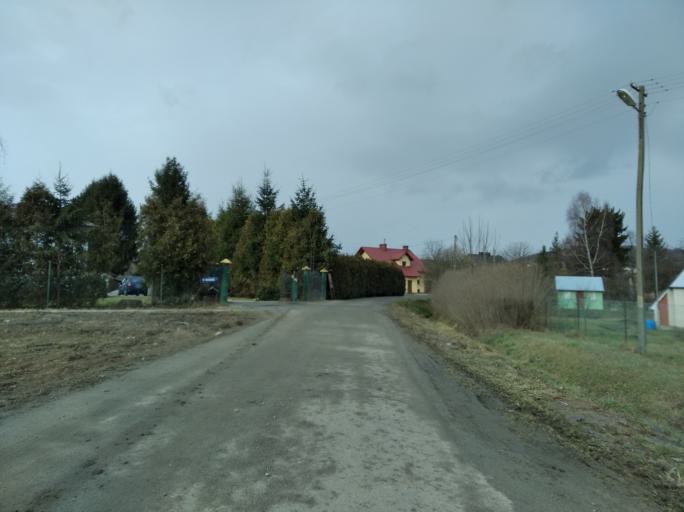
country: PL
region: Subcarpathian Voivodeship
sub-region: Powiat strzyzowski
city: Strzyzow
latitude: 49.8637
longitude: 21.7825
